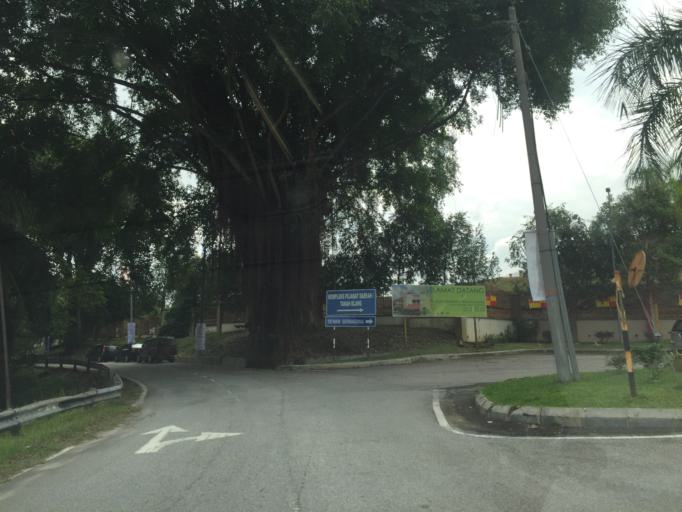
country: MY
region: Selangor
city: Klang
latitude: 3.0408
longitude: 101.4438
